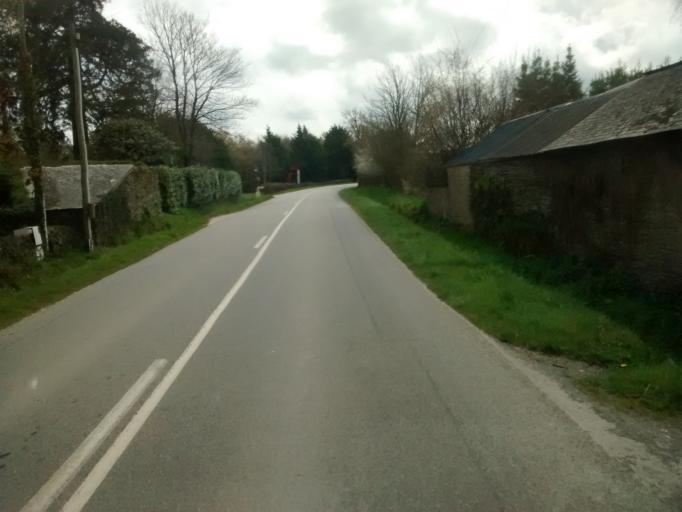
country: FR
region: Brittany
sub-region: Departement du Morbihan
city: Ploermel
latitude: 47.9024
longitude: -2.3736
